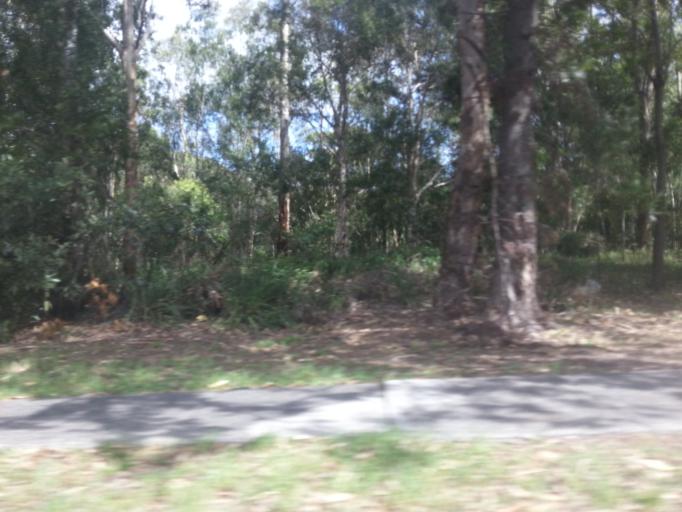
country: AU
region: New South Wales
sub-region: Wollongong
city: Gwynneville
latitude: -34.4194
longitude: 150.8842
